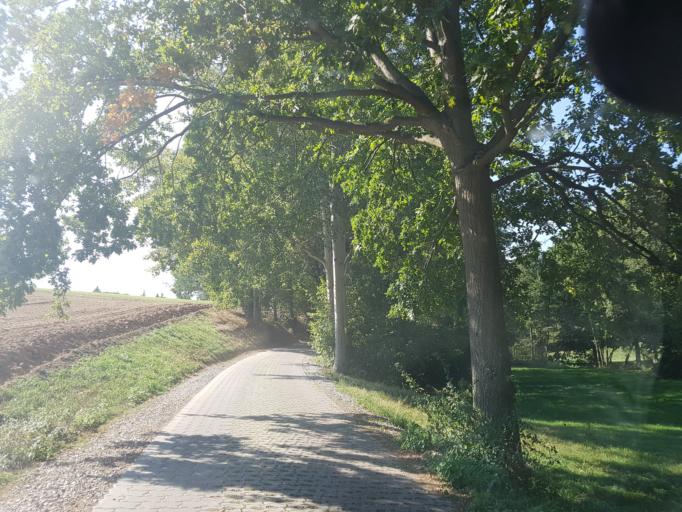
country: DE
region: Saxony
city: Kriebstein
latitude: 51.0471
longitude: 12.9832
